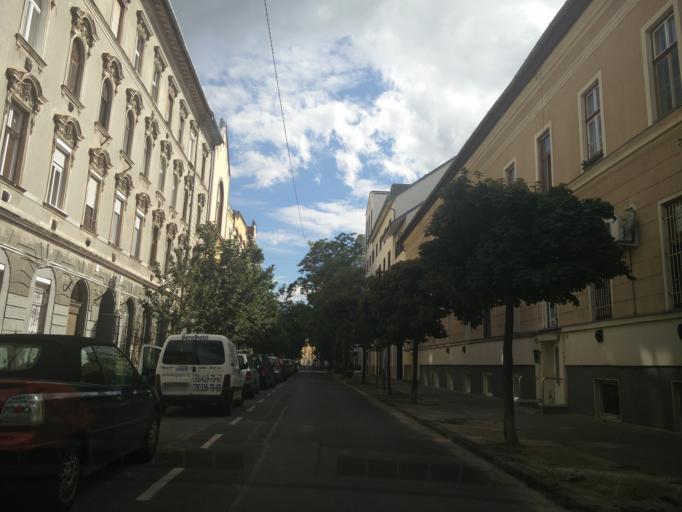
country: HU
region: Budapest
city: Budapest XIII. keruelet
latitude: 47.5258
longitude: 19.0656
